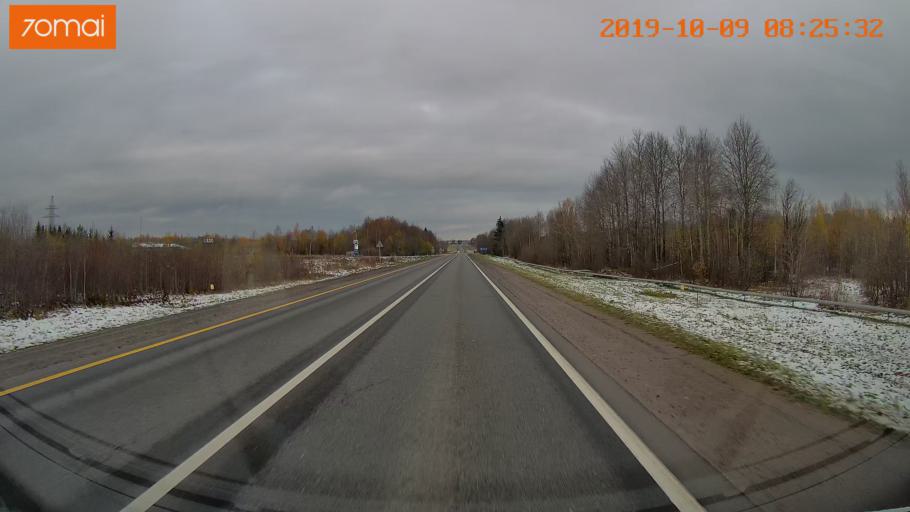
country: RU
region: Vologda
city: Gryazovets
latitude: 58.7826
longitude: 40.2717
